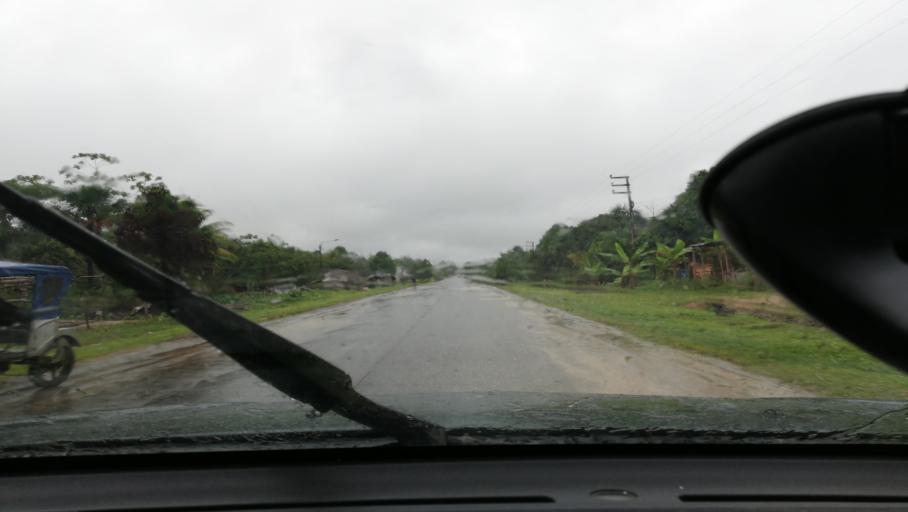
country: PE
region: Loreto
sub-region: Provincia de Maynas
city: San Juan
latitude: -4.0945
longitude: -73.4533
